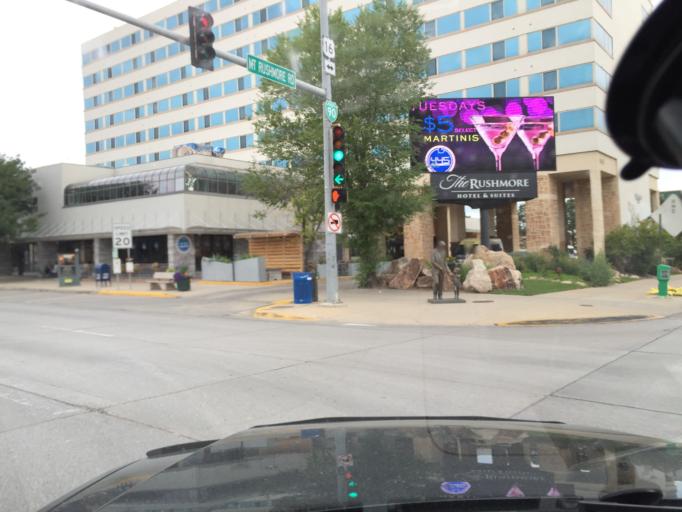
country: US
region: South Dakota
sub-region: Pennington County
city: Rapid City
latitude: 44.0816
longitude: -103.2308
